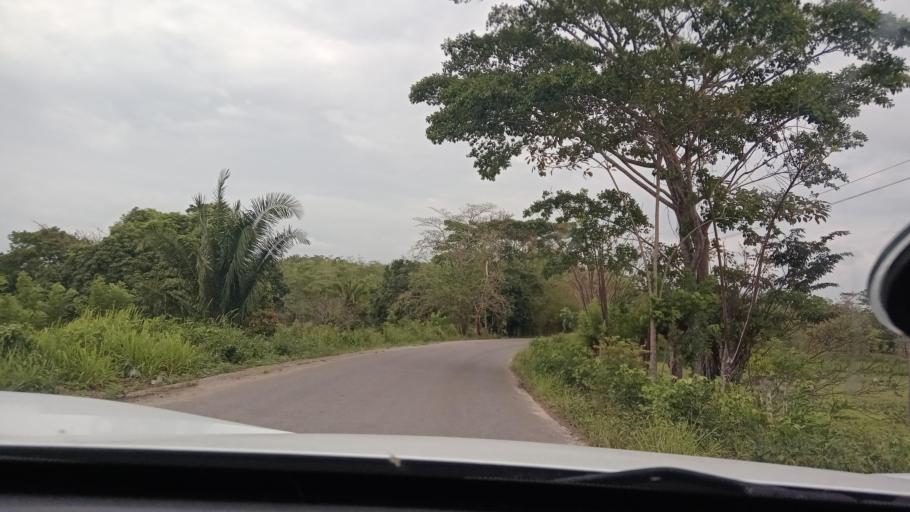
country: MX
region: Tabasco
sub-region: Huimanguillo
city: Francisco Rueda
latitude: 17.5856
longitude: -94.0927
